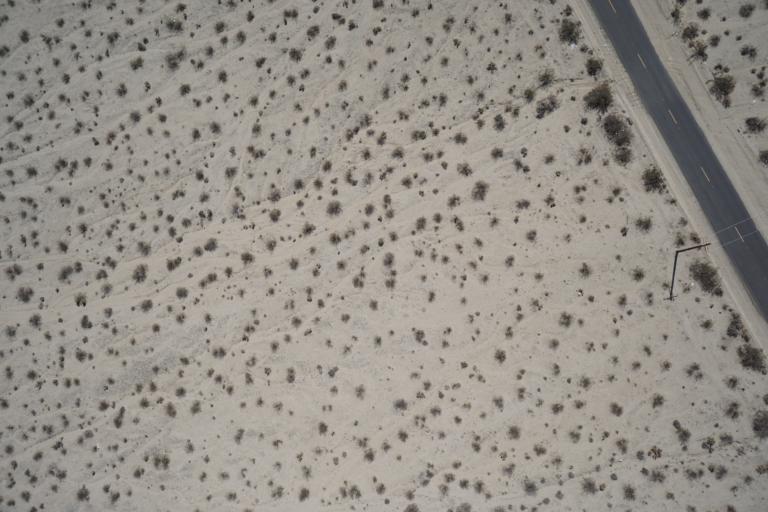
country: US
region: California
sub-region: San Bernardino County
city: Twentynine Palms
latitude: 34.1221
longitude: -116.0231
